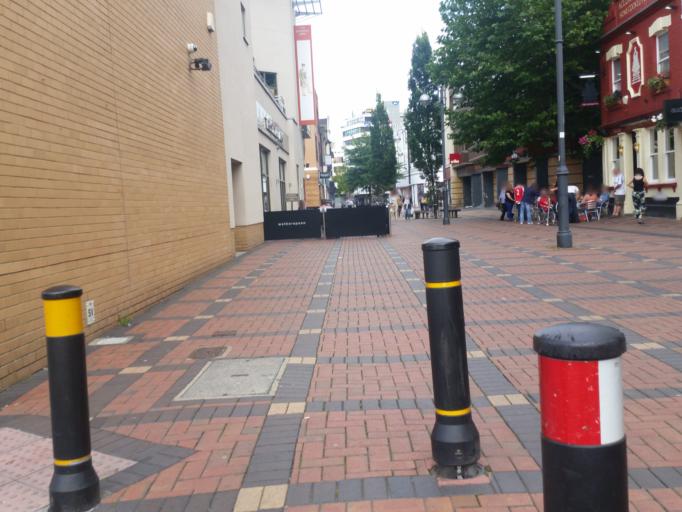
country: GB
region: England
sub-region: Borough of Swindon
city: Swindon
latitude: 51.5621
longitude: -1.7881
